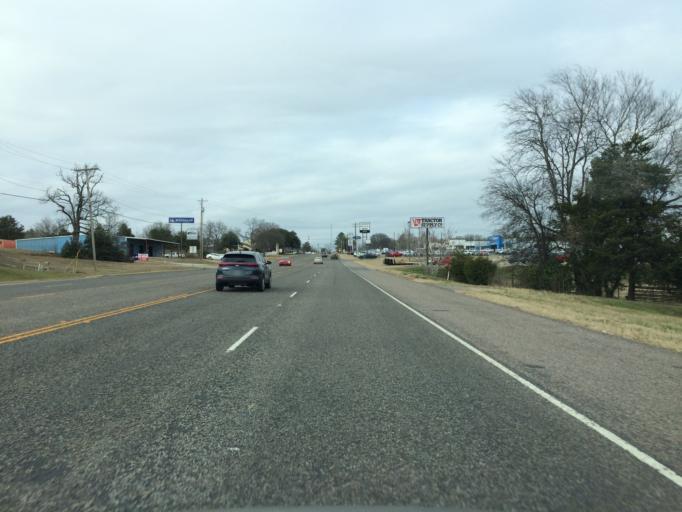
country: US
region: Texas
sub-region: Wood County
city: Mineola
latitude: 32.6494
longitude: -95.4902
